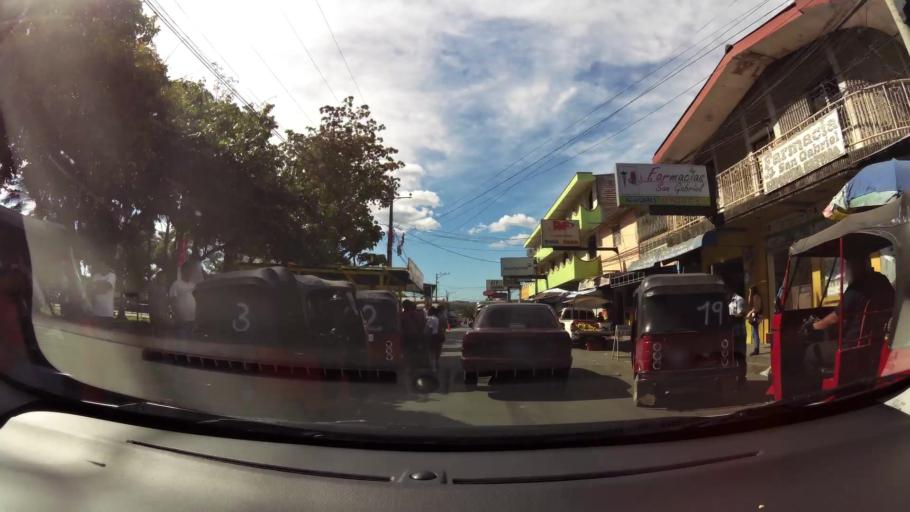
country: SV
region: San Salvador
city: Aguilares
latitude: 13.9578
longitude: -89.1869
